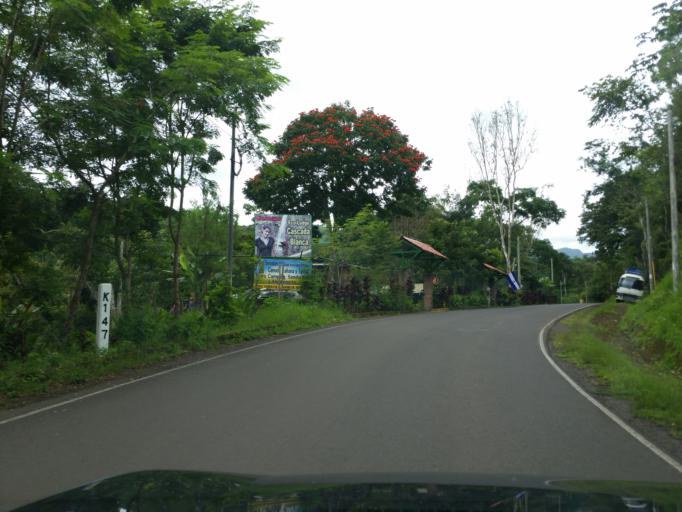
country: NI
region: Matagalpa
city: San Ramon
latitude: 12.9920
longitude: -85.8294
